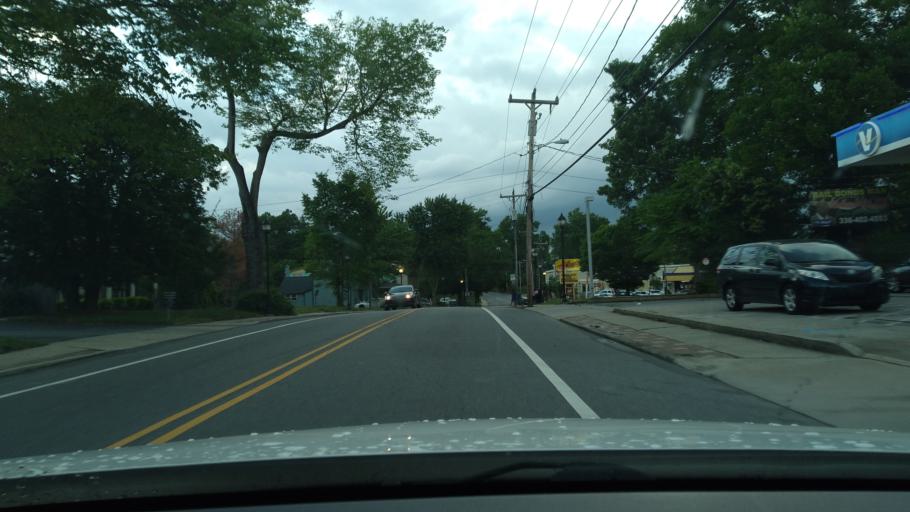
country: US
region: North Carolina
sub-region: Guilford County
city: Greensboro
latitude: 36.0605
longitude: -79.7851
